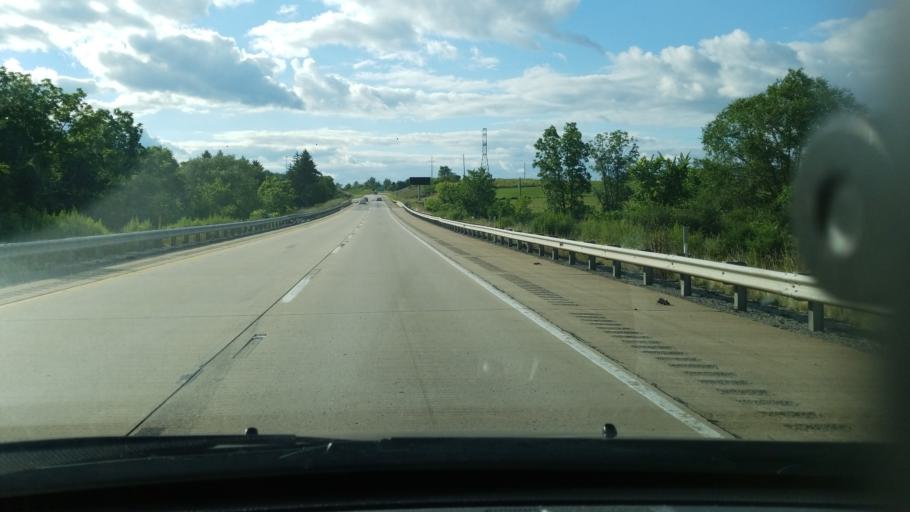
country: US
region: Pennsylvania
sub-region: Northumberland County
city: Milton
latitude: 40.9979
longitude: -76.7462
